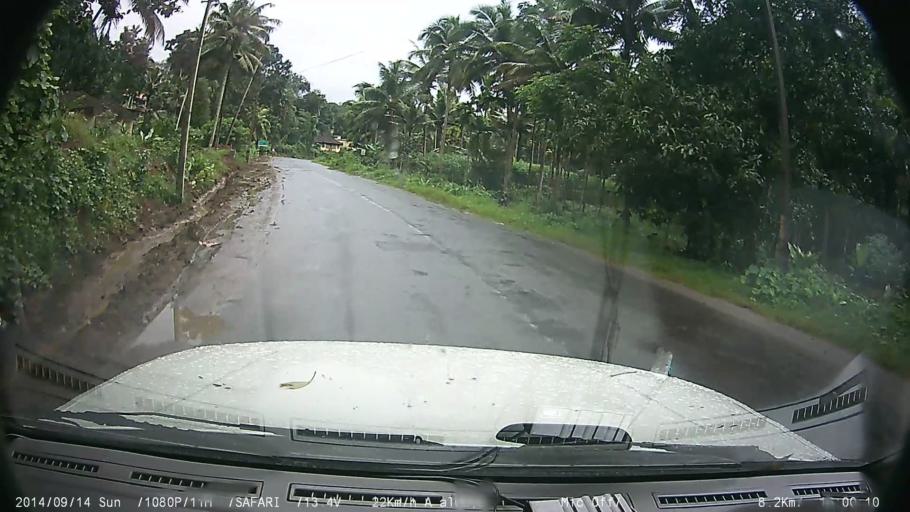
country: IN
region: Kerala
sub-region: Kottayam
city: Palackattumala
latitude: 9.7748
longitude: 76.5723
